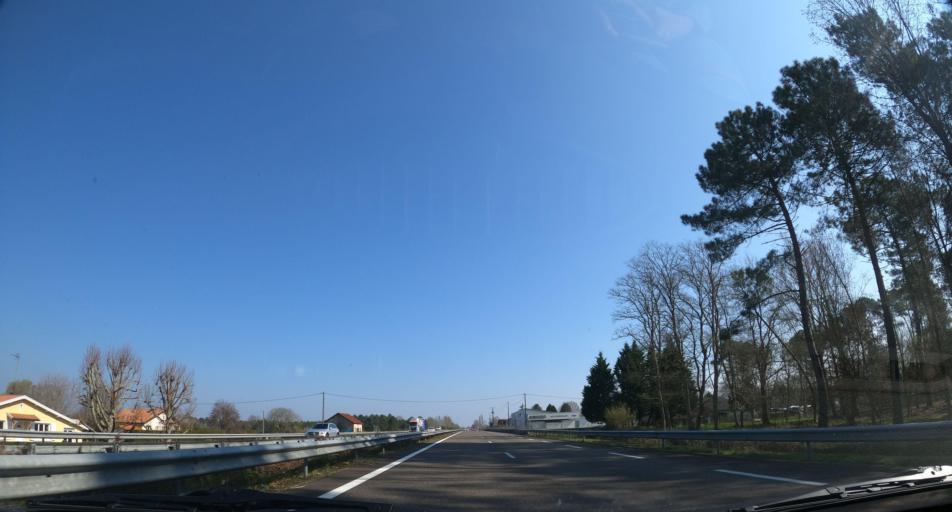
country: FR
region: Aquitaine
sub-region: Departement des Landes
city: Meilhan
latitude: 43.8554
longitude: -0.7282
